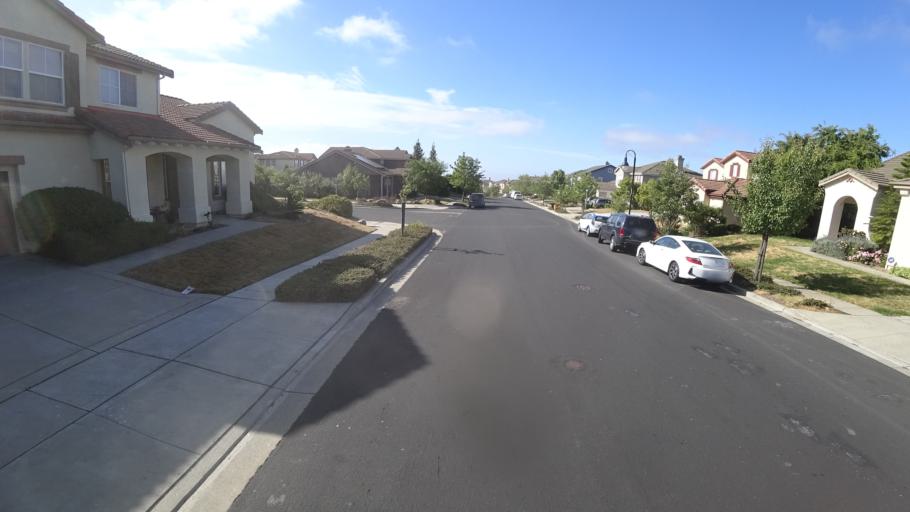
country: US
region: California
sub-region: Alameda County
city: Fairview
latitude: 37.6498
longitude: -122.0191
